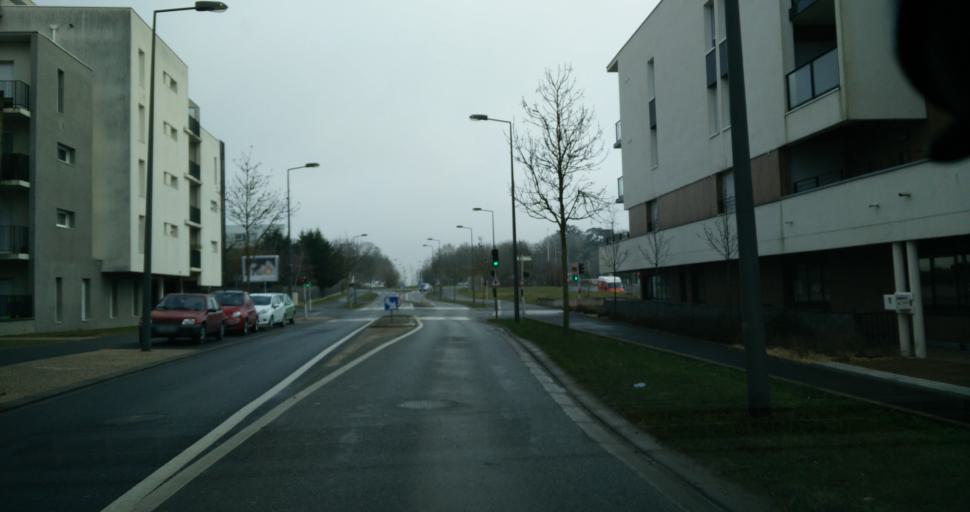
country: FR
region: Centre
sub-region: Departement d'Indre-et-Loire
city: Saint-Cyr-sur-Loire
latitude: 47.4189
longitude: 0.7020
